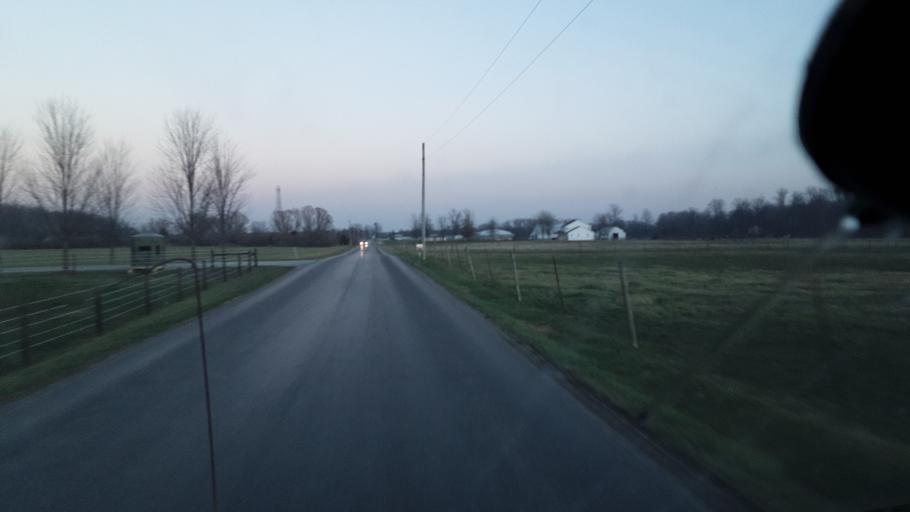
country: US
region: Indiana
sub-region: Allen County
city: Grabill
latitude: 41.2391
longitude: -84.9379
